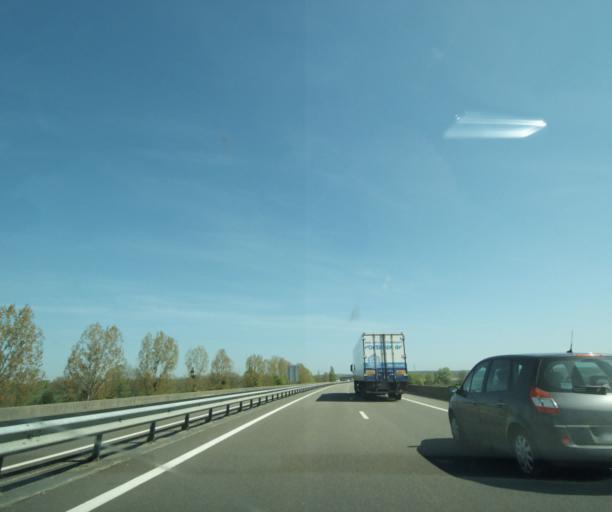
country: FR
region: Bourgogne
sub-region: Departement de la Nievre
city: Sermoise-sur-Loire
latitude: 46.9661
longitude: 3.1827
